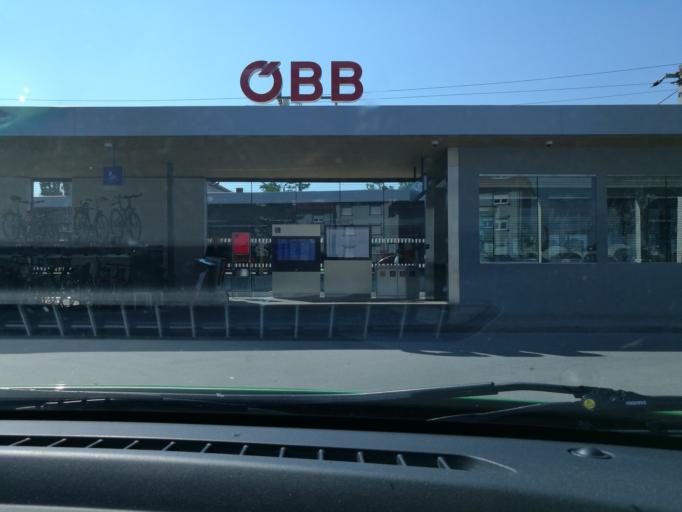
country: AT
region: Lower Austria
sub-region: Politischer Bezirk Ganserndorf
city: Ganserndorf
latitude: 48.3406
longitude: 16.7321
